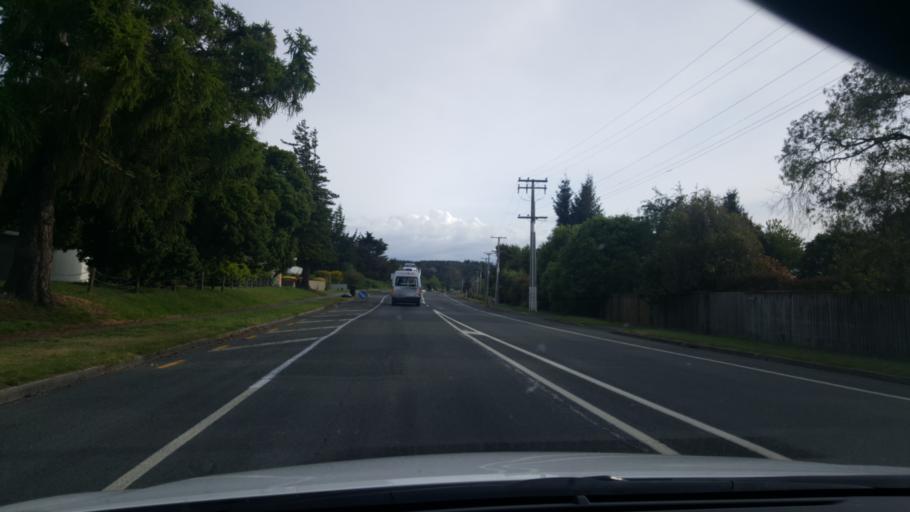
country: NZ
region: Waikato
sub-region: Taupo District
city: Taupo
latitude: -38.7878
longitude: 176.0765
